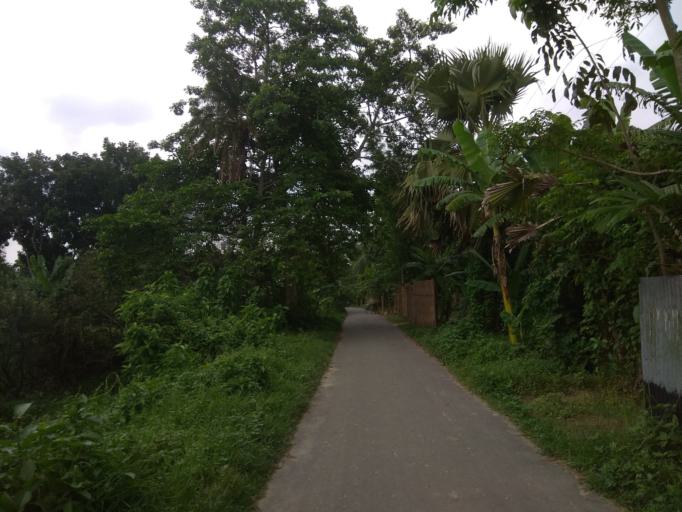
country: BD
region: Dhaka
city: Dohar
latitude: 23.4883
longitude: 89.9961
